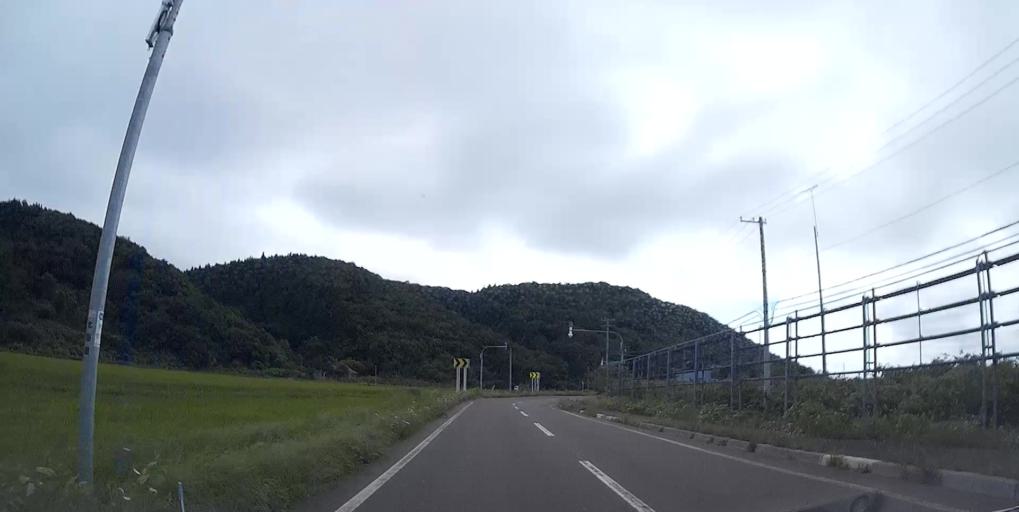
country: JP
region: Hokkaido
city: Kamiiso
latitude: 41.9725
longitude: 140.1564
